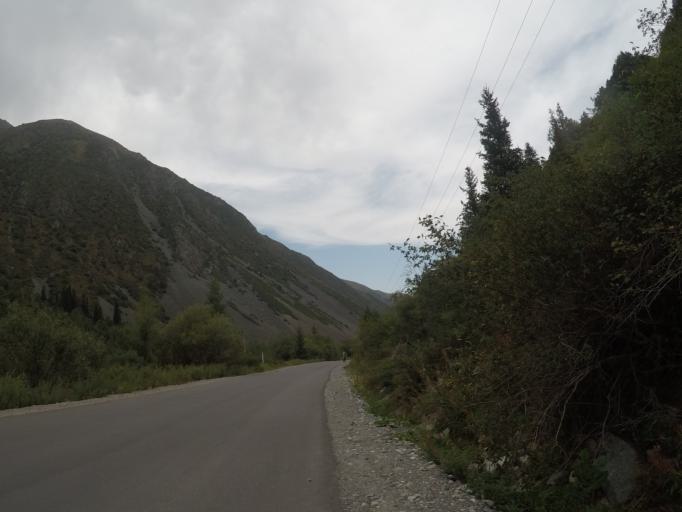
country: KG
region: Chuy
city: Bishkek
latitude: 42.5764
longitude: 74.4820
